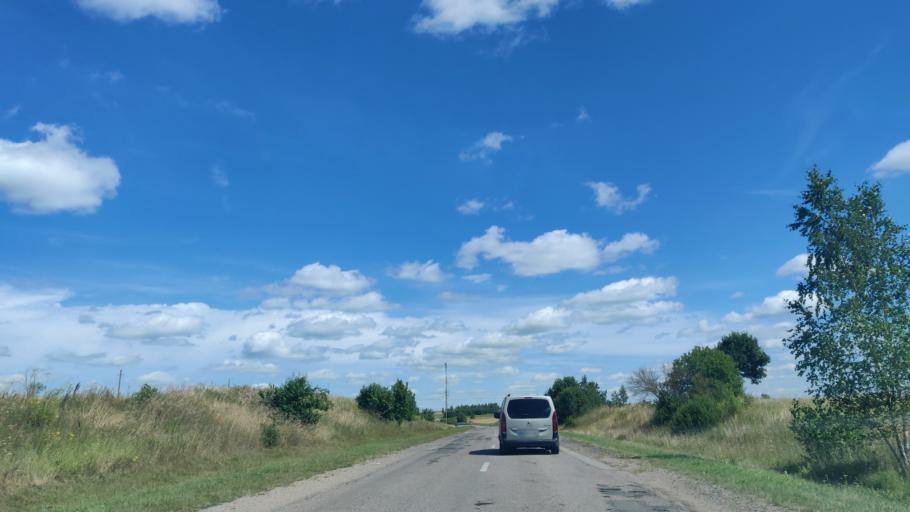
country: LT
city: Salcininkai
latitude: 54.4566
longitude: 25.4852
